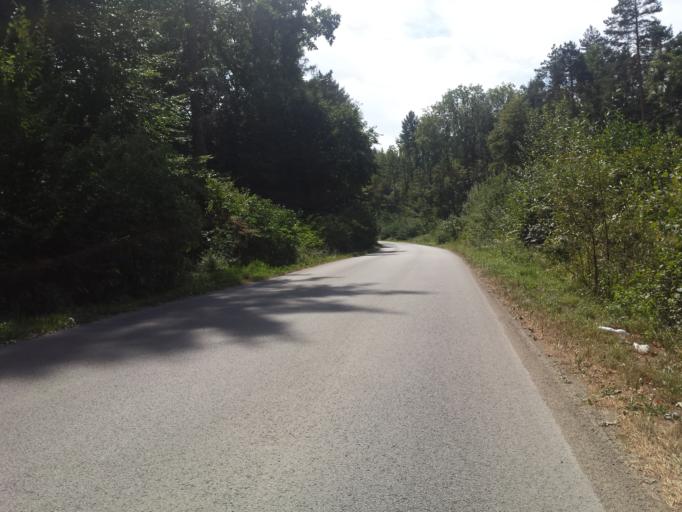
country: PL
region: Subcarpathian Voivodeship
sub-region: Powiat przemyski
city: Fredropol
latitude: 49.6652
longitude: 22.7247
